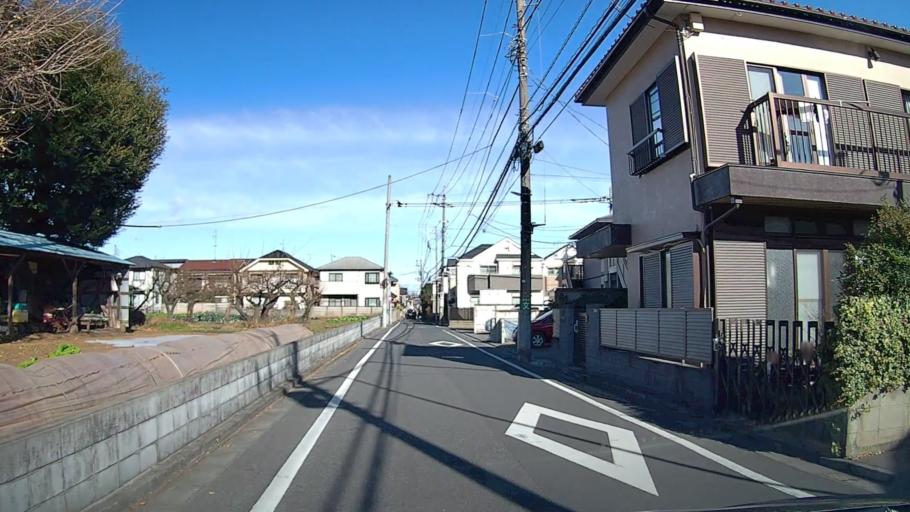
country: JP
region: Saitama
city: Wako
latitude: 35.7553
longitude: 139.6123
